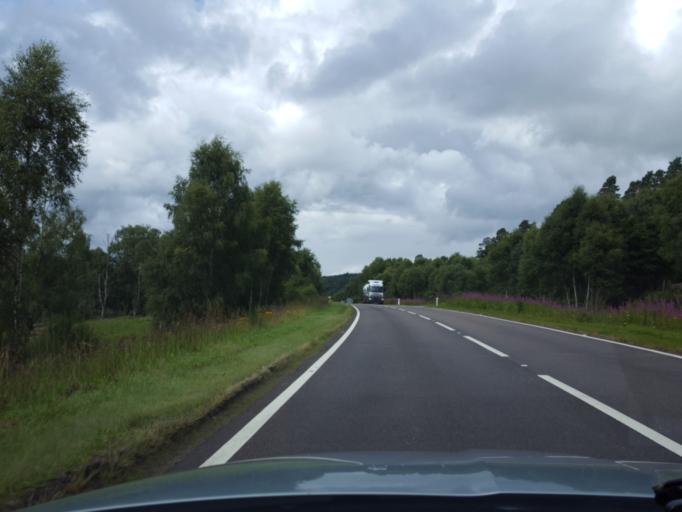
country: GB
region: Scotland
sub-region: Highland
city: Grantown on Spey
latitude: 57.2818
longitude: -3.6810
